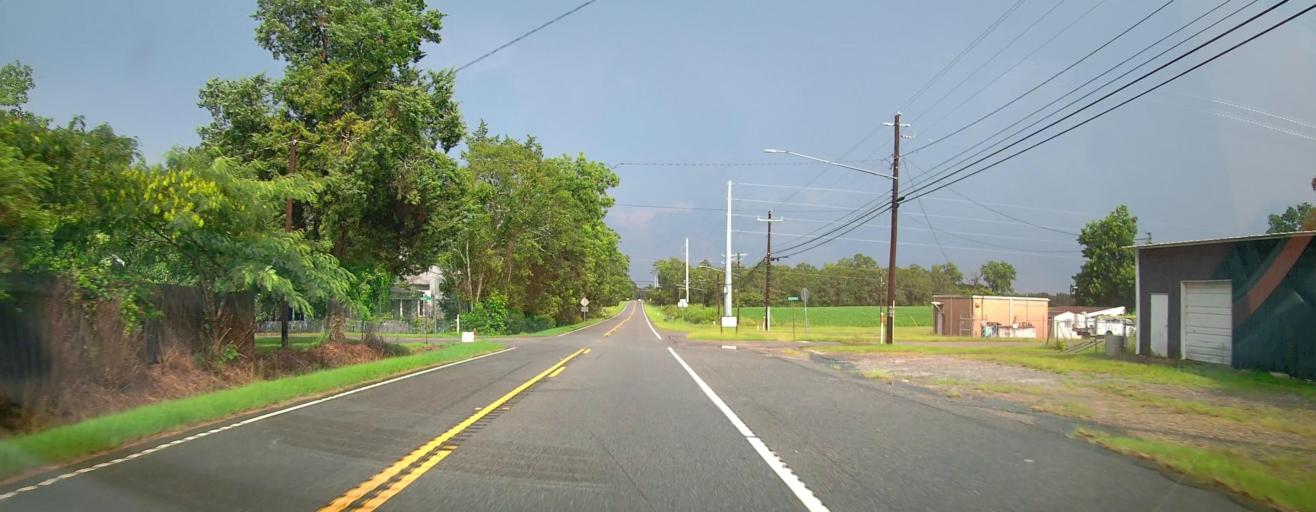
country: US
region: Georgia
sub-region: Twiggs County
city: Jeffersonville
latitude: 32.6033
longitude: -83.2482
